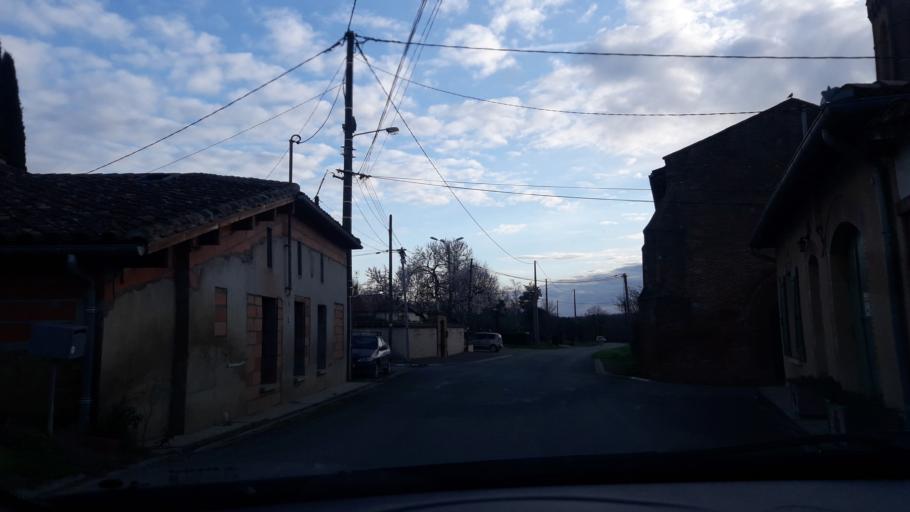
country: FR
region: Midi-Pyrenees
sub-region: Departement de la Haute-Garonne
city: Levignac
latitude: 43.6621
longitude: 1.1680
